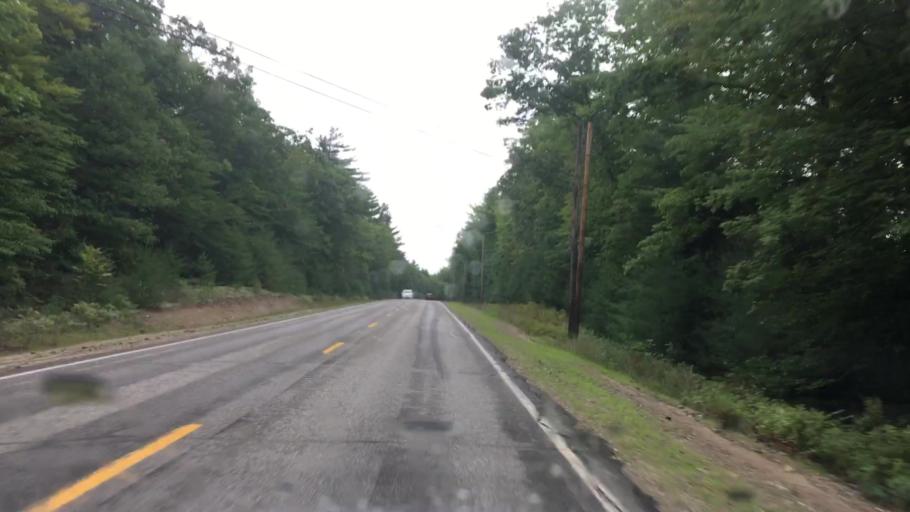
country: US
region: Maine
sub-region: Oxford County
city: Fryeburg
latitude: 43.9986
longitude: -70.9426
